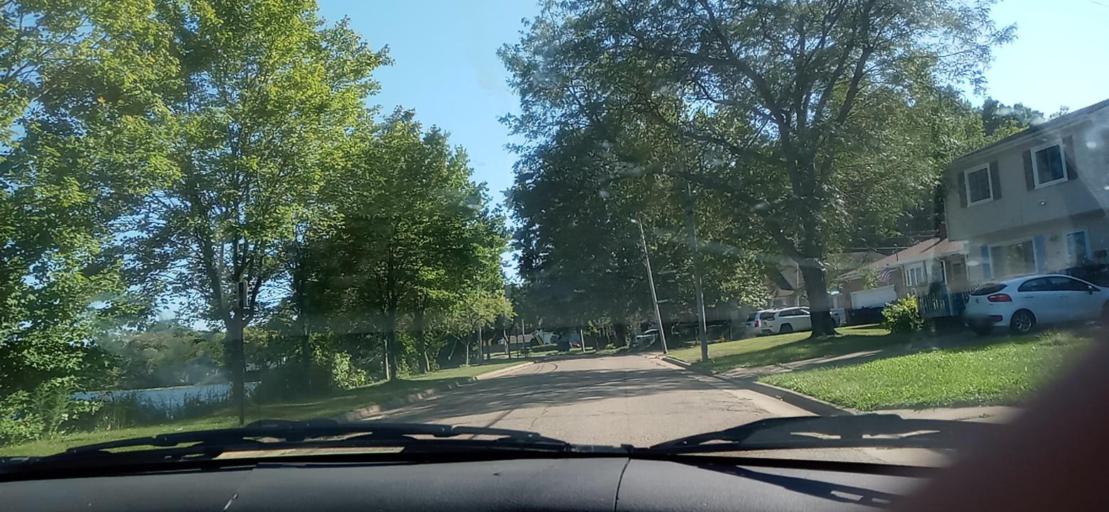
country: US
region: Ohio
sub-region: Summit County
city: Akron
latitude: 41.0529
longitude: -81.5470
